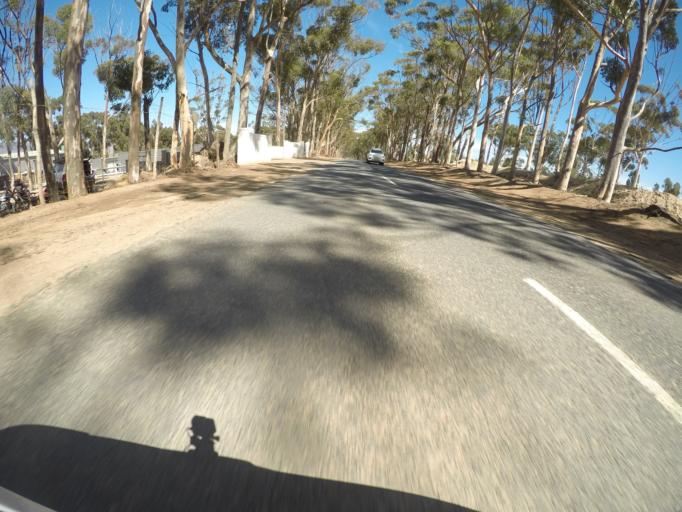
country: ZA
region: Western Cape
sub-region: City of Cape Town
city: Sunset Beach
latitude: -33.7627
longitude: 18.5519
